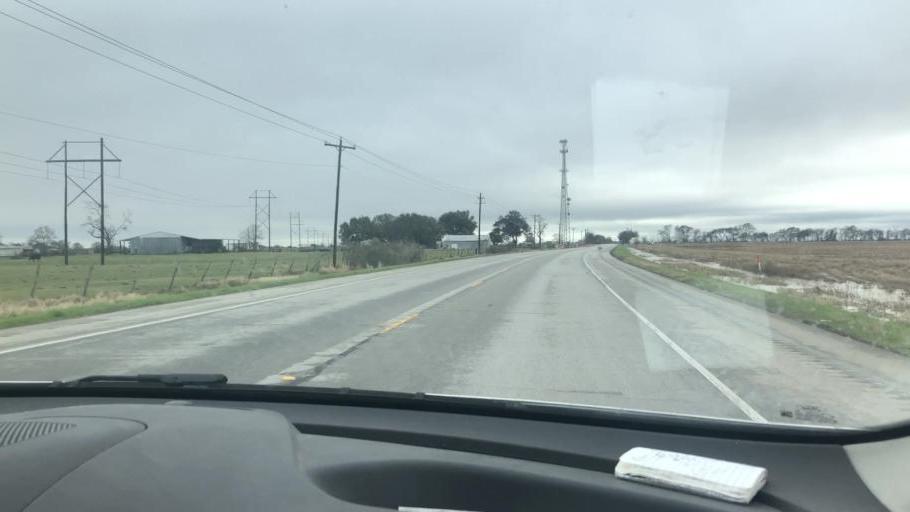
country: US
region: Texas
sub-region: Wharton County
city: Boling
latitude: 29.1420
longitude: -95.9854
